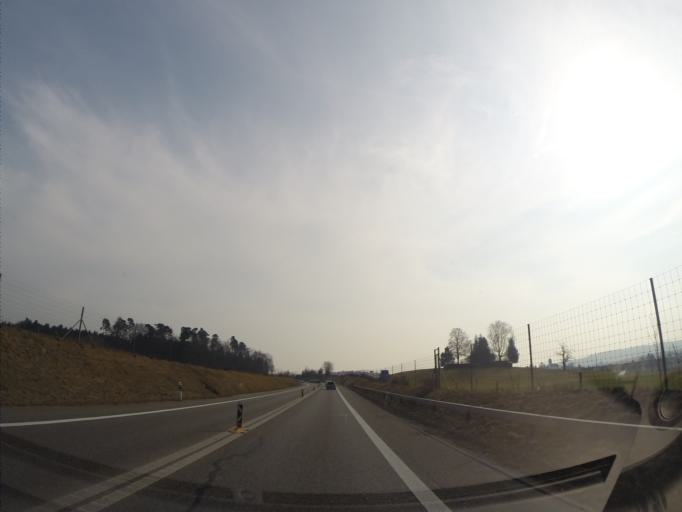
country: CH
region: Zurich
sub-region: Bezirk Andelfingen
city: Henggart
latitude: 47.5690
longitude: 8.6887
